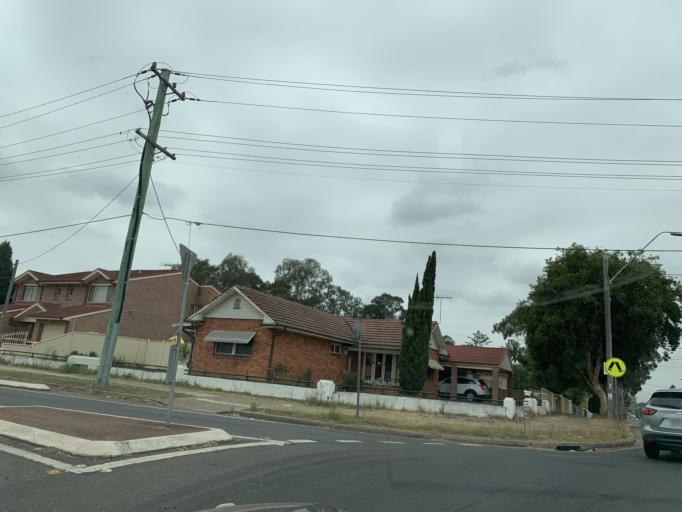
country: AU
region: New South Wales
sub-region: Blacktown
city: Doonside
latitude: -33.7561
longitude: 150.8709
